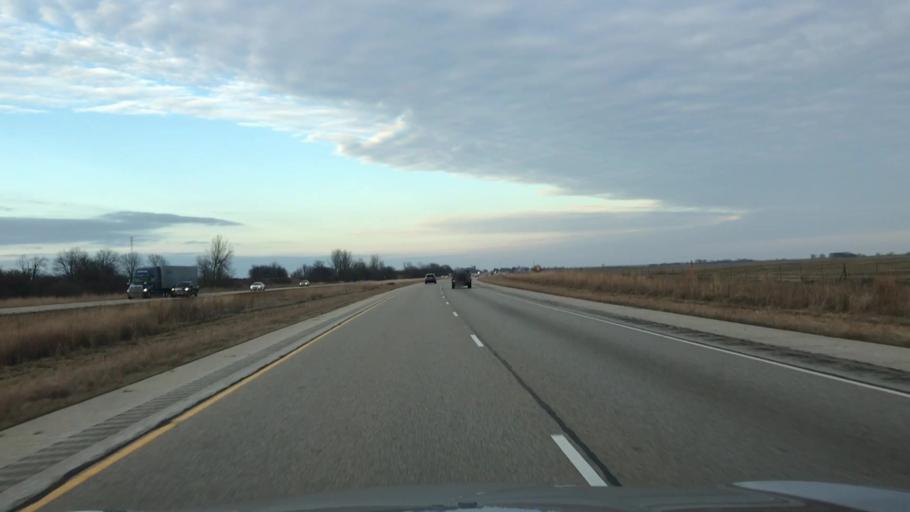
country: US
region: Illinois
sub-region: McLean County
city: Twin Grove
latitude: 40.3790
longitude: -89.0930
